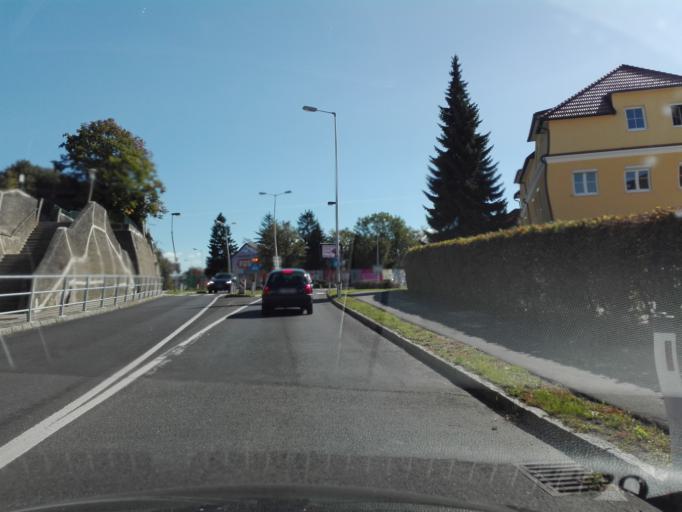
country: AT
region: Upper Austria
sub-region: Politischer Bezirk Linz-Land
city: Enns
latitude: 48.2118
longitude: 14.4765
